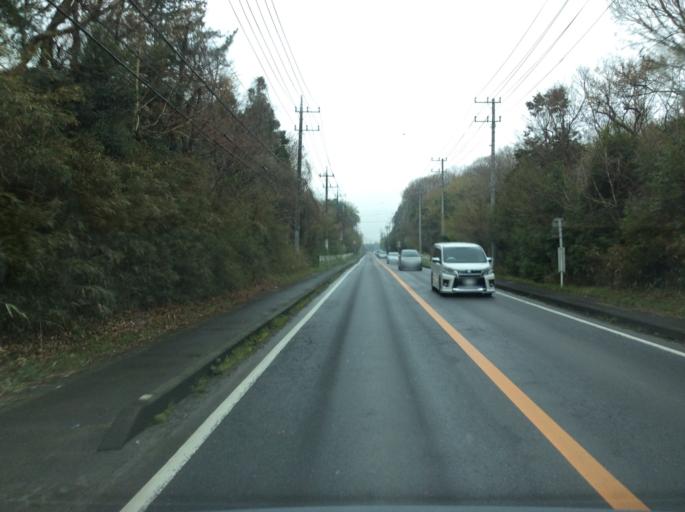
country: JP
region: Ibaraki
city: Mitsukaido
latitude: 35.9849
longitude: 139.9574
